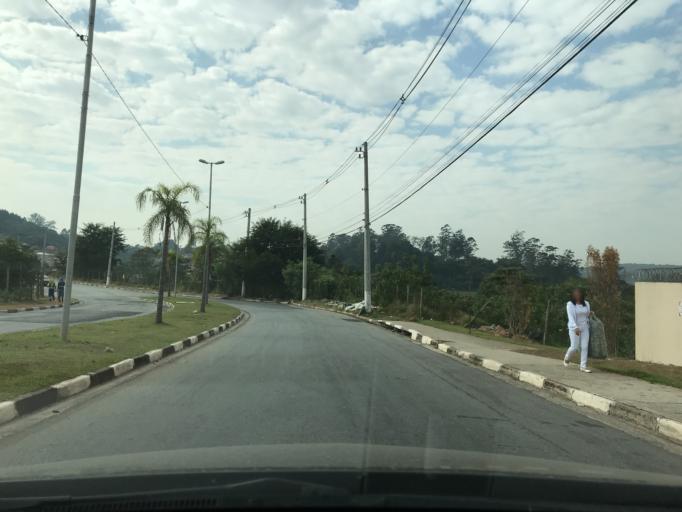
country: BR
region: Sao Paulo
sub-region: Cotia
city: Cotia
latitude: -23.6153
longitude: -46.9252
